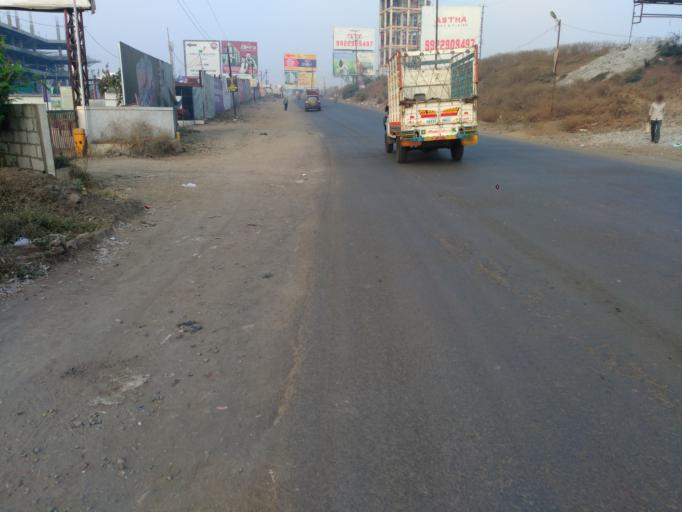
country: IN
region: Maharashtra
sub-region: Pune Division
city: Pune
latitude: 18.4500
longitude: 73.9132
